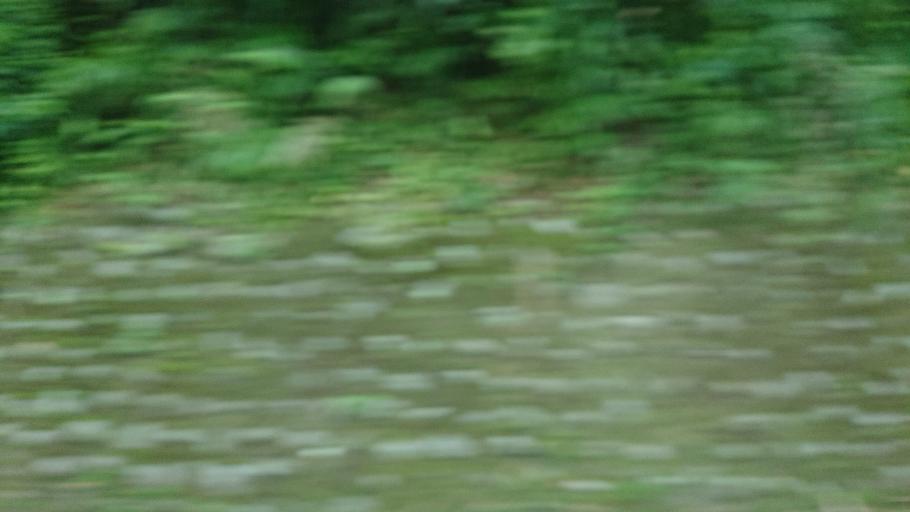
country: TW
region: Taiwan
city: Daxi
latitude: 24.8904
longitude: 121.3769
